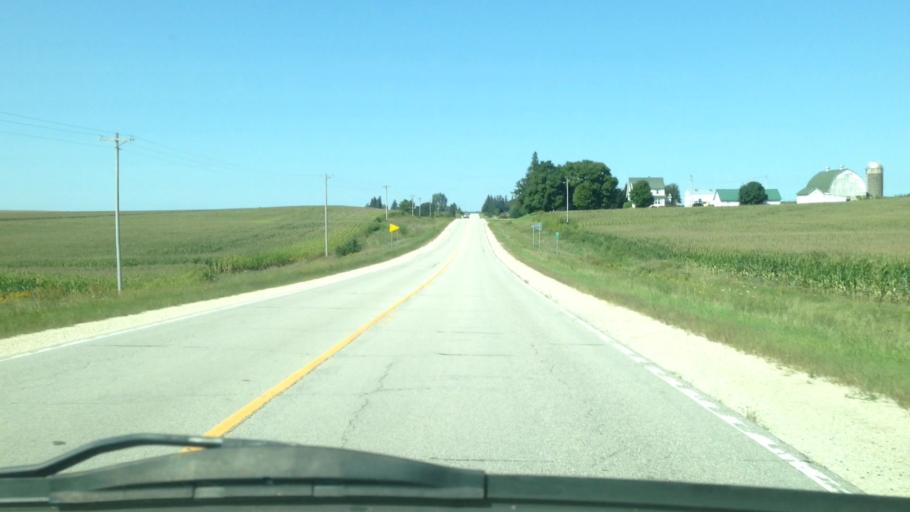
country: US
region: Minnesota
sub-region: Houston County
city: Spring Grove
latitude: 43.6097
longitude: -91.7904
